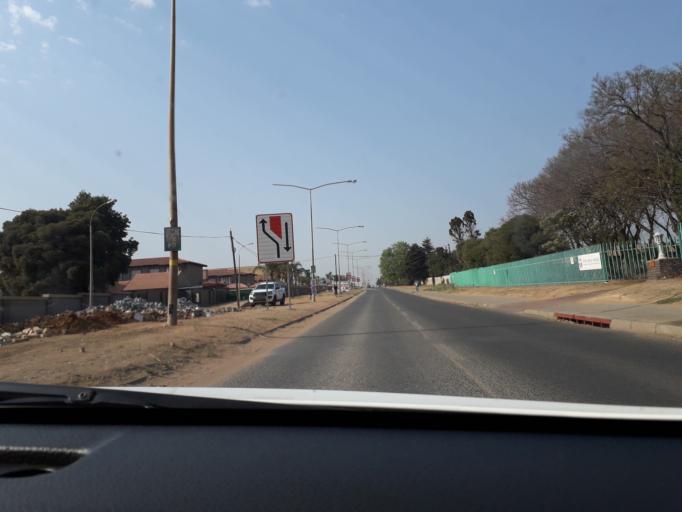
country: ZA
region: Gauteng
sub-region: Ekurhuleni Metropolitan Municipality
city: Tembisa
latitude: -26.0746
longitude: 28.2474
